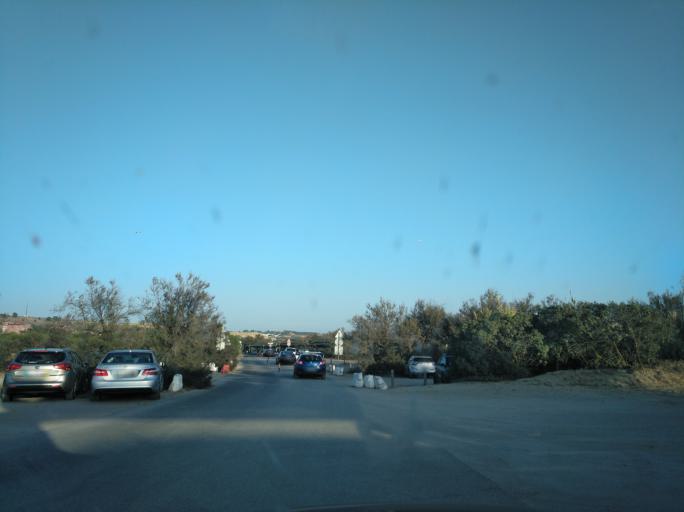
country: PT
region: Setubal
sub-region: Almada
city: Trafaria
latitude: 38.6606
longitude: -9.2540
